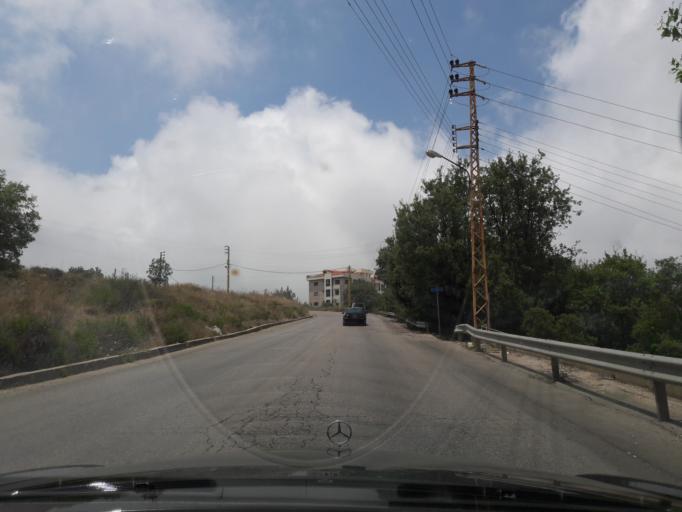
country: LB
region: Mont-Liban
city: Djounie
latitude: 33.9166
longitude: 35.6869
